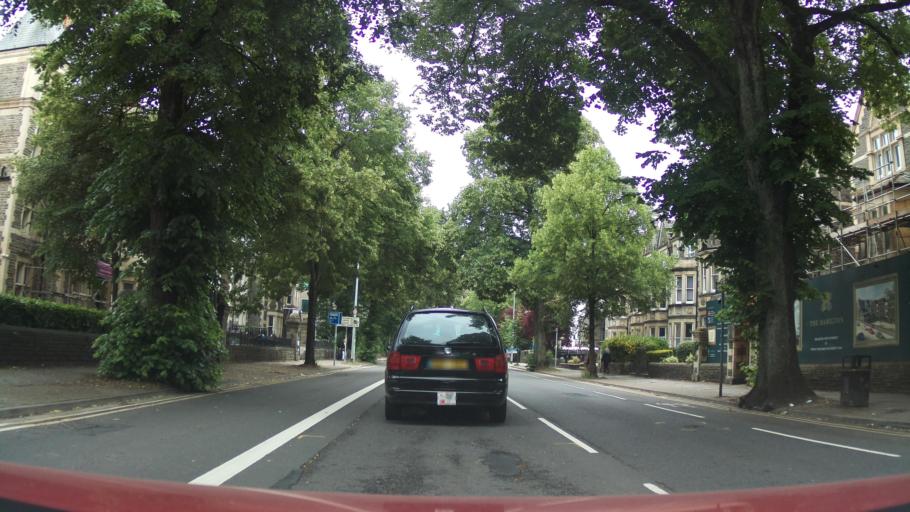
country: GB
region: Wales
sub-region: Cardiff
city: Cardiff
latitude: 51.4836
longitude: -3.1913
